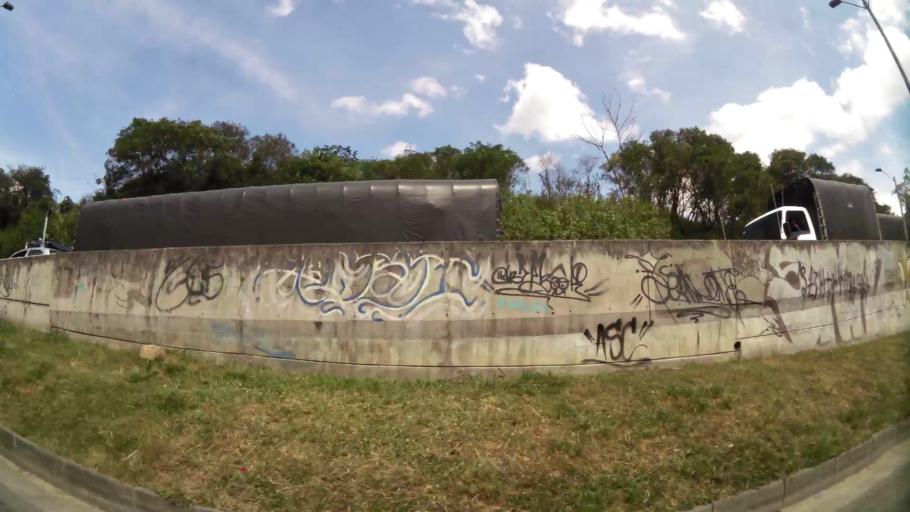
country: CO
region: Antioquia
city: Bello
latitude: 6.2964
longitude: -75.5614
